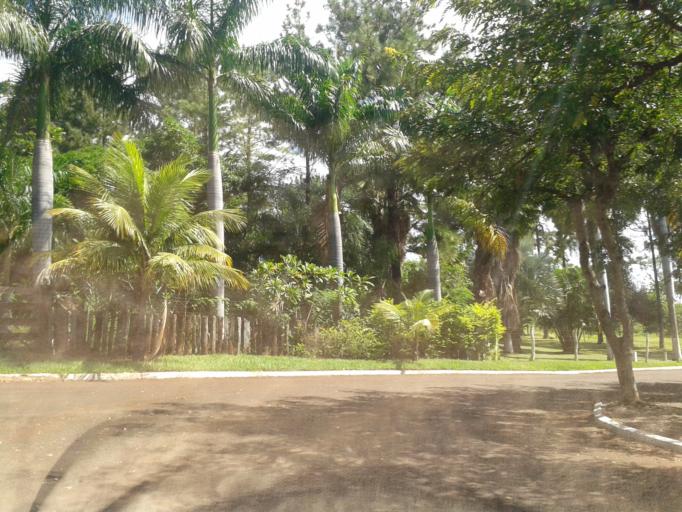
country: BR
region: Minas Gerais
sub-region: Capinopolis
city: Capinopolis
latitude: -18.5247
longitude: -49.4985
